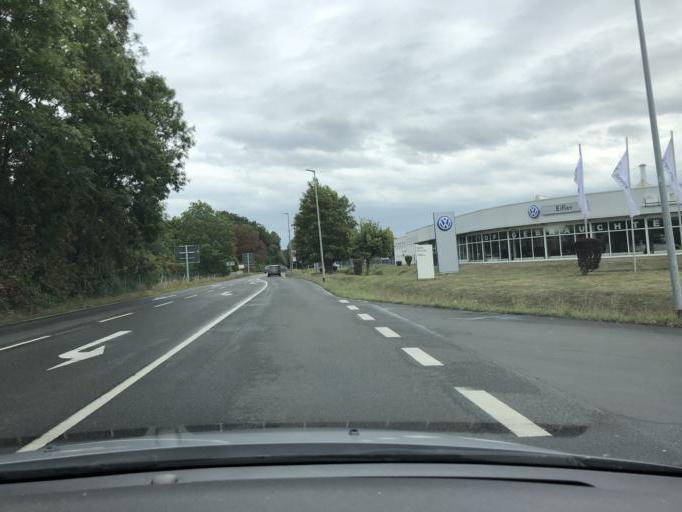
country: DE
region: Saxony-Anhalt
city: Koethen
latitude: 51.7557
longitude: 11.9458
